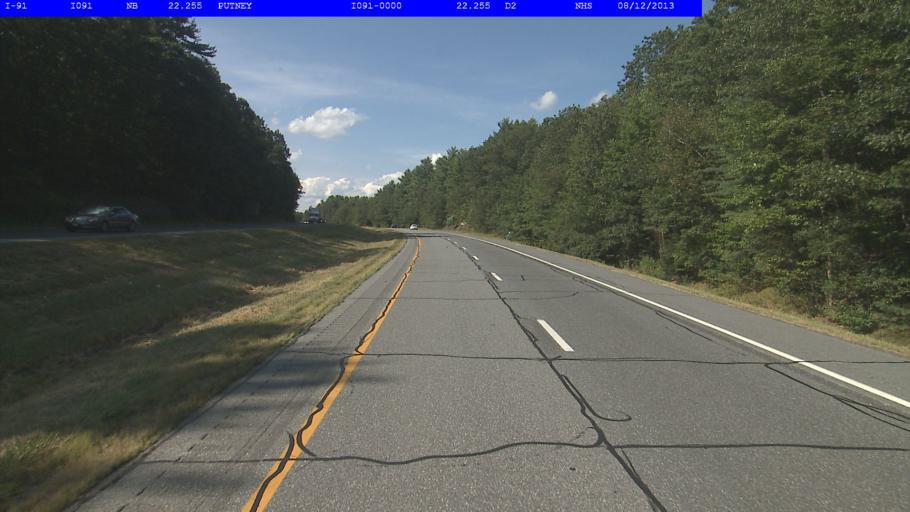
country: US
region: New Hampshire
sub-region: Cheshire County
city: Westmoreland
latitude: 43.0021
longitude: -72.4681
